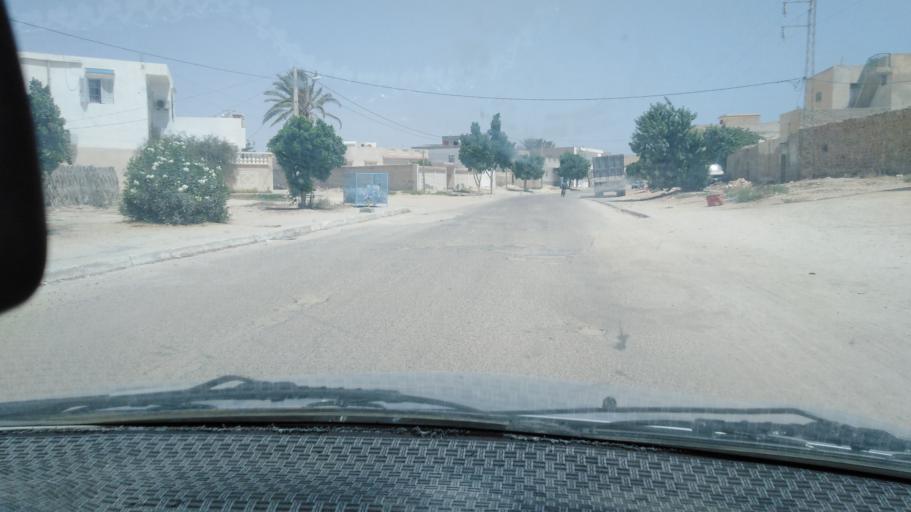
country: TN
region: Qabis
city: Gabes
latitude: 33.9578
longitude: 9.9955
